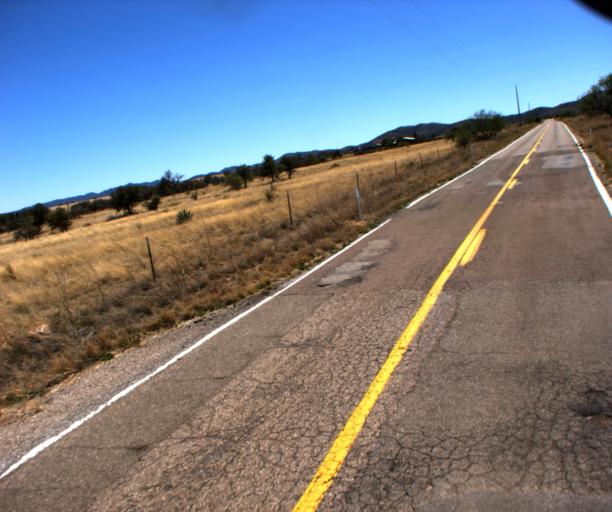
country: US
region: Arizona
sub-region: Cochise County
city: Huachuca City
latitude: 31.5982
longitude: -110.5580
